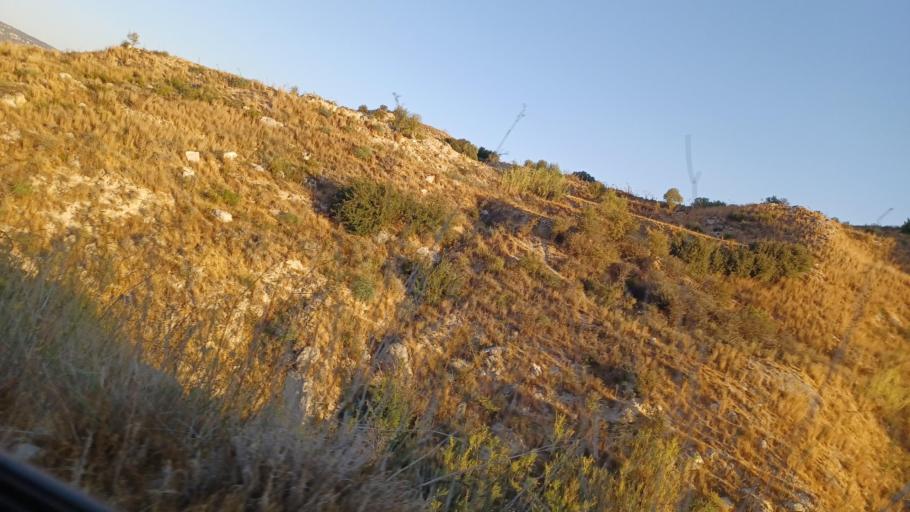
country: CY
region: Pafos
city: Tala
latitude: 34.9066
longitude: 32.5126
